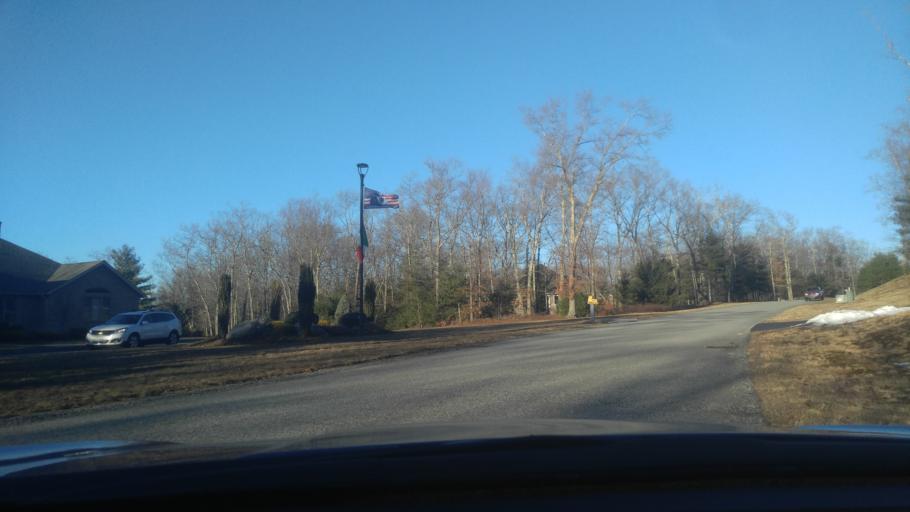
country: US
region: Rhode Island
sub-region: Kent County
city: West Warwick
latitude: 41.6468
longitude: -71.5589
